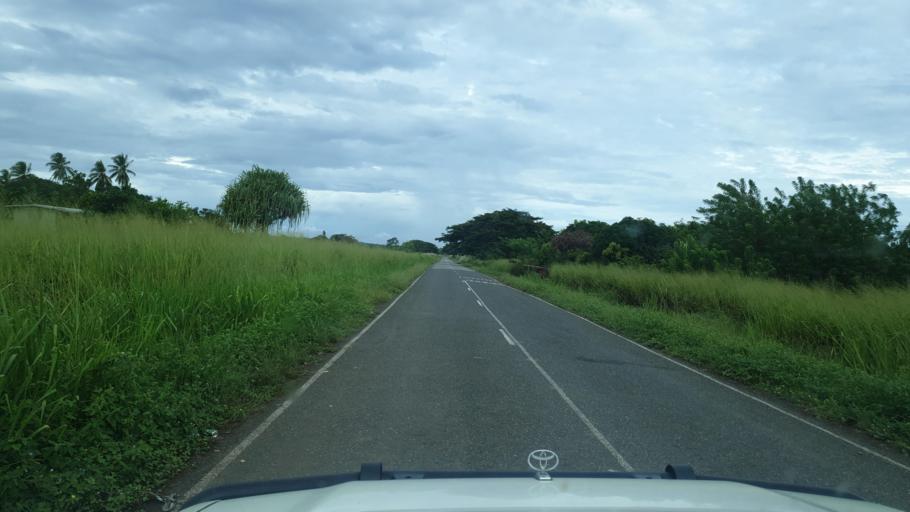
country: PG
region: National Capital
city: Port Moresby
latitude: -9.0163
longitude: 146.8468
